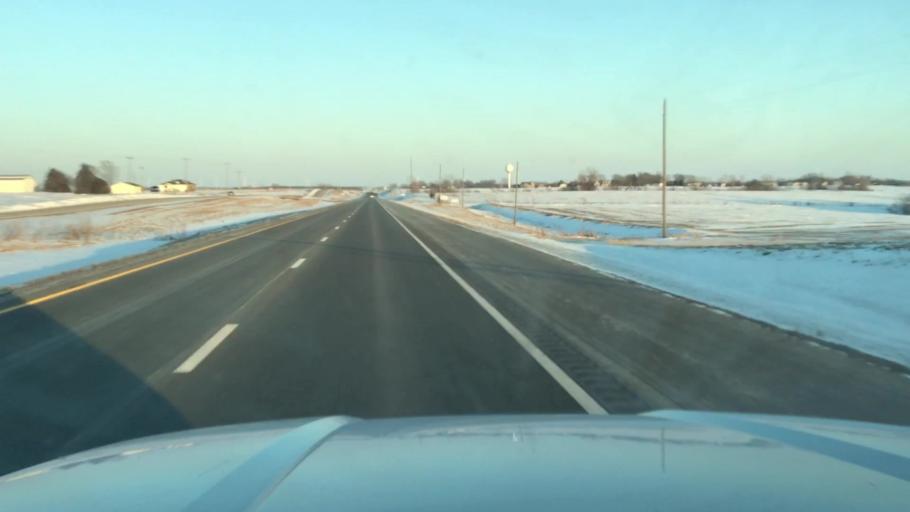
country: US
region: Missouri
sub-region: Clinton County
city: Gower
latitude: 39.7620
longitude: -94.5207
